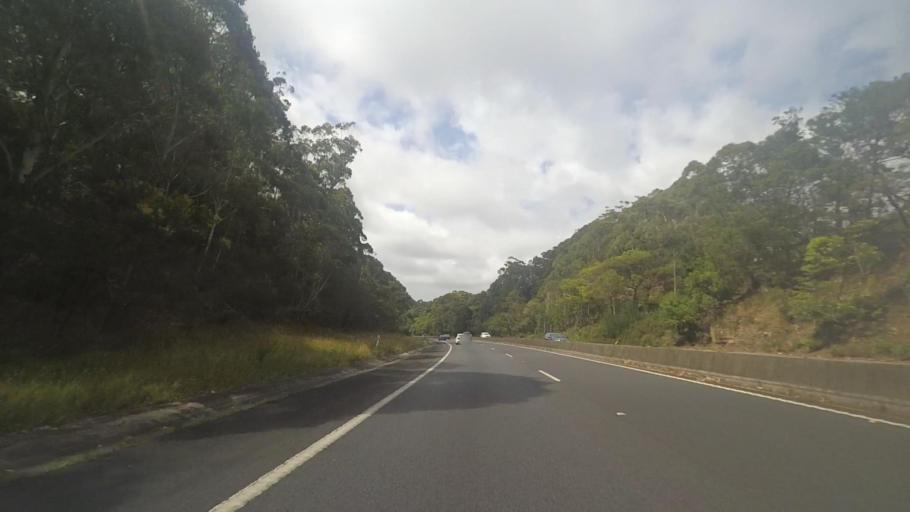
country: AU
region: New South Wales
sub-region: Wollongong
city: Bulli
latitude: -34.3277
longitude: 150.8765
